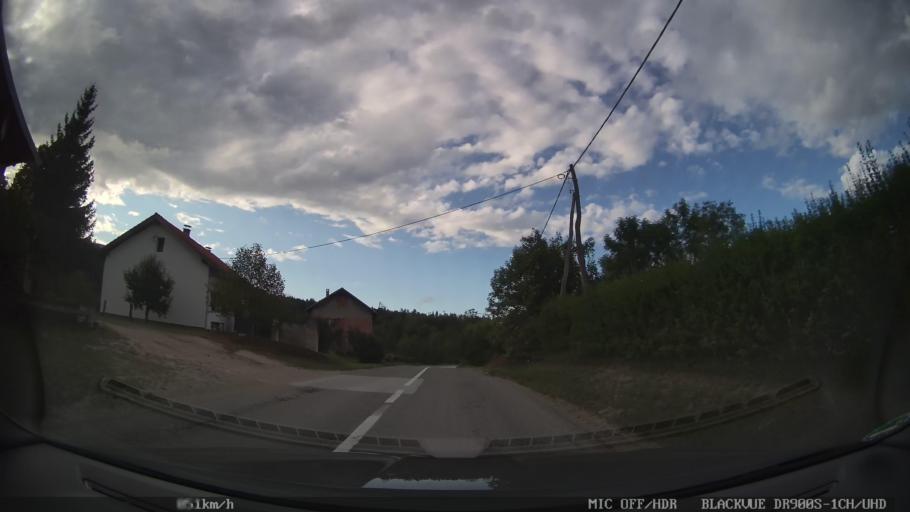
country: HR
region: Karlovacka
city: Plaski
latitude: 44.9969
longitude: 15.4258
